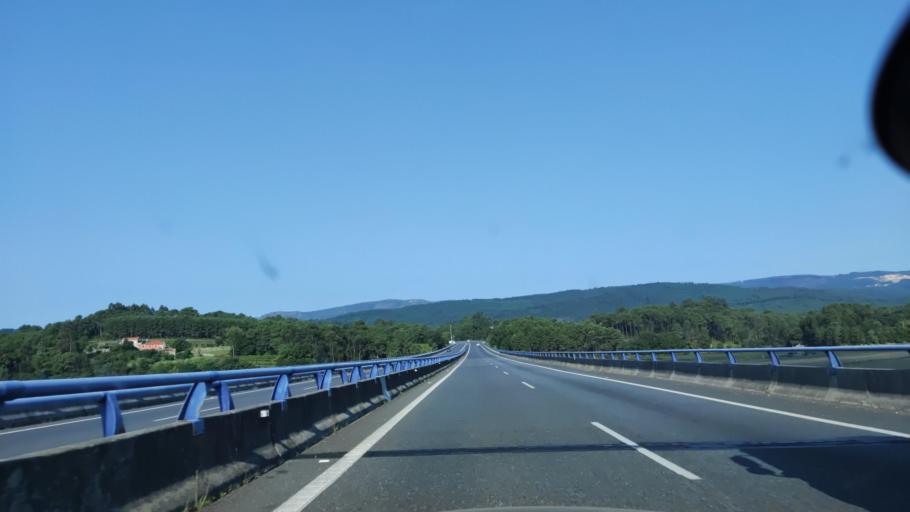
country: ES
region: Galicia
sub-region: Provincia da Coruna
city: Rianxo
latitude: 42.6744
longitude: -8.8354
